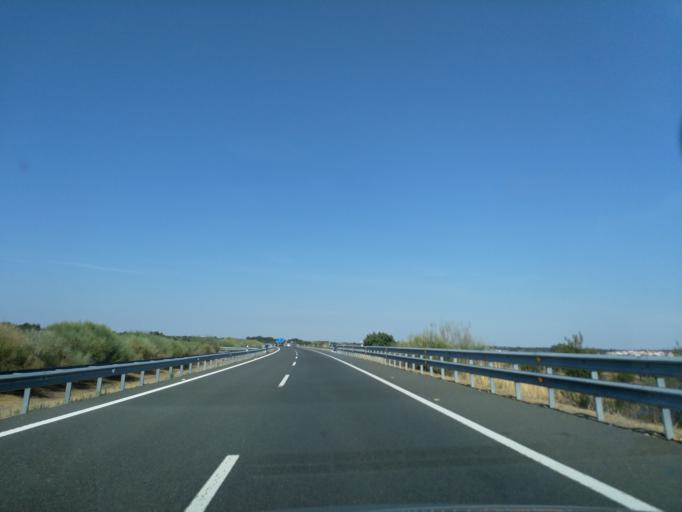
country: ES
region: Extremadura
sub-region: Provincia de Caceres
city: Casas de Don Antonio
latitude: 39.2160
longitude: -6.2895
